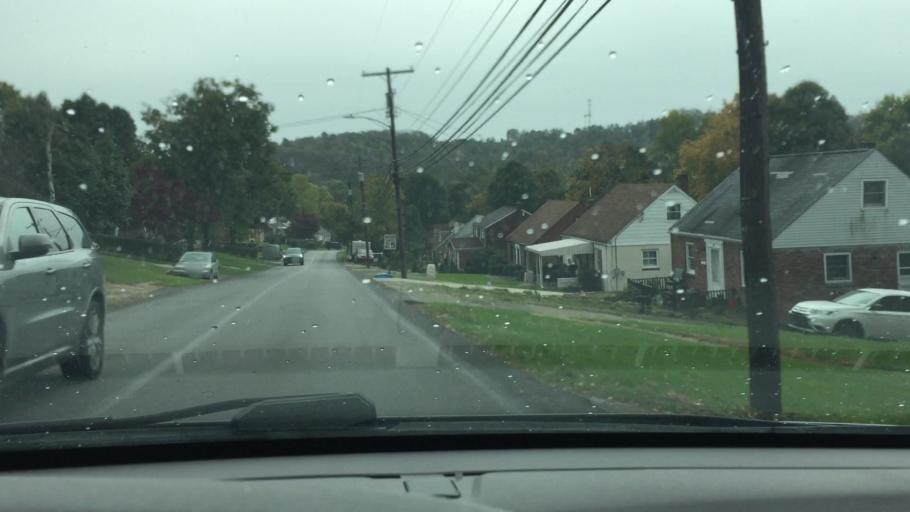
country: US
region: Pennsylvania
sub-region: Washington County
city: Canonsburg
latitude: 40.2588
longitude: -80.1633
